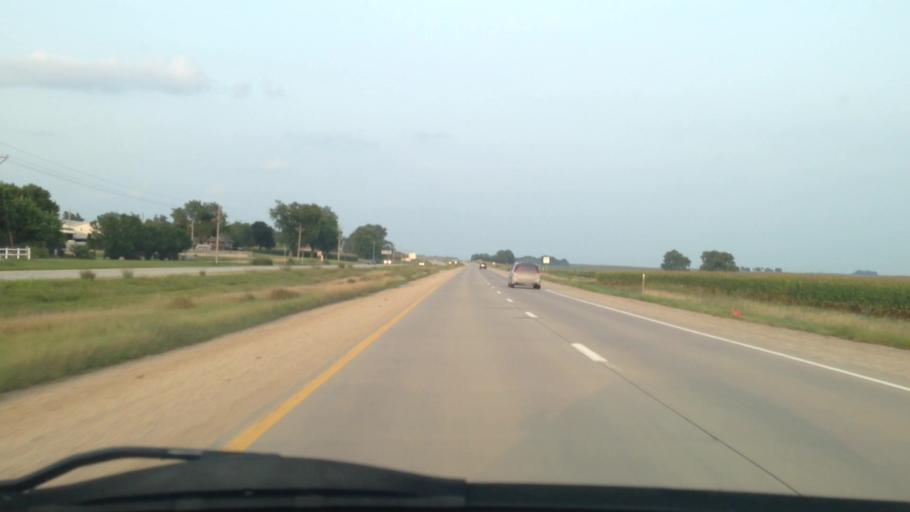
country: US
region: Iowa
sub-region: Benton County
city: Atkins
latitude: 41.9634
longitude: -91.8701
